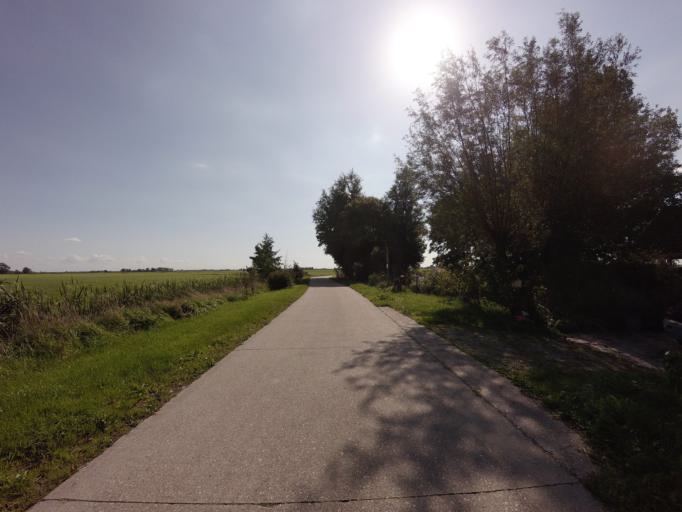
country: NL
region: Friesland
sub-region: Gemeente Littenseradiel
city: Makkum
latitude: 53.0981
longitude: 5.6485
